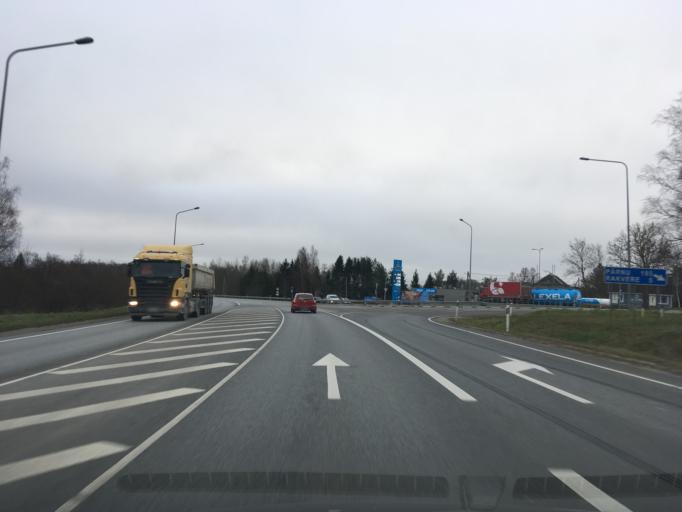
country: EE
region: Laeaene-Virumaa
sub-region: Someru vald
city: Someru
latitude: 59.3662
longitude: 26.4323
